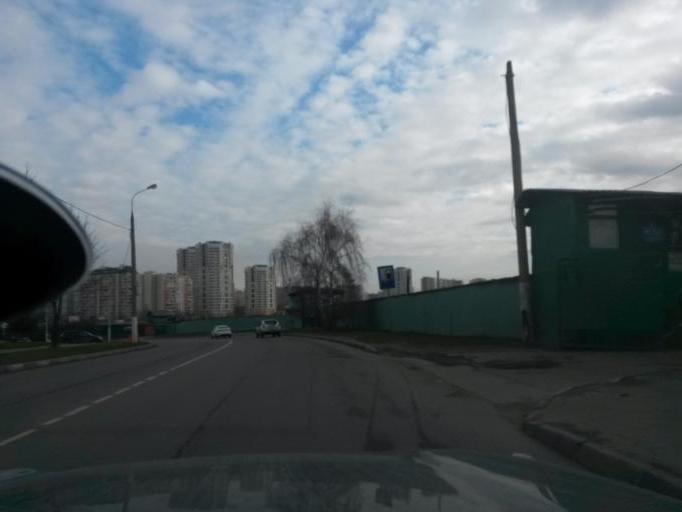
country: RU
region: Moscow
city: Brateyevo
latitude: 55.6270
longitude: 37.7511
